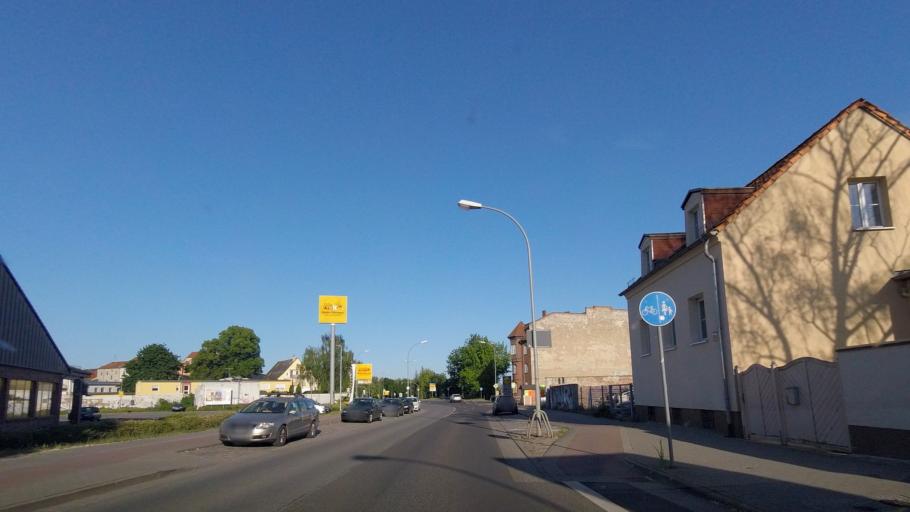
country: DE
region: Brandenburg
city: Brandenburg an der Havel
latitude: 52.4061
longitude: 12.5700
